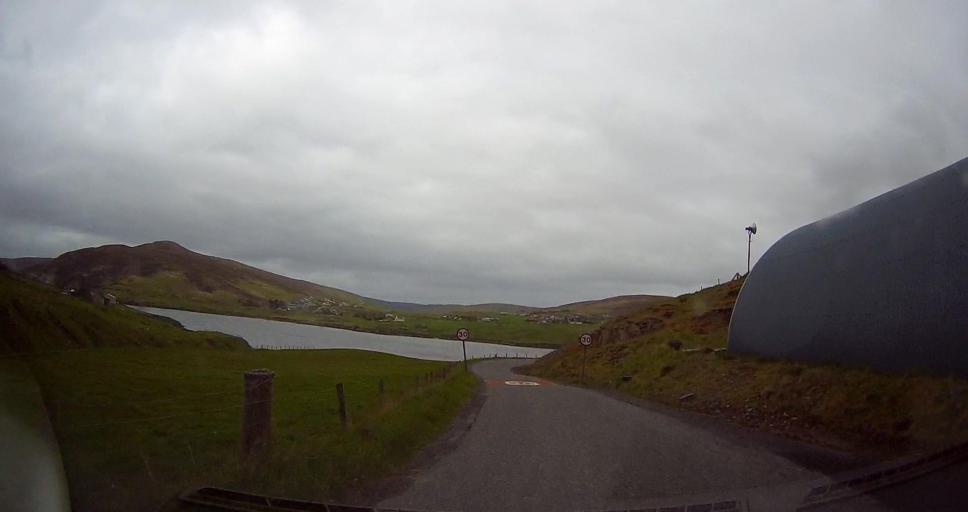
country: GB
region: Scotland
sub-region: Shetland Islands
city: Lerwick
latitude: 60.3465
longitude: -1.2713
